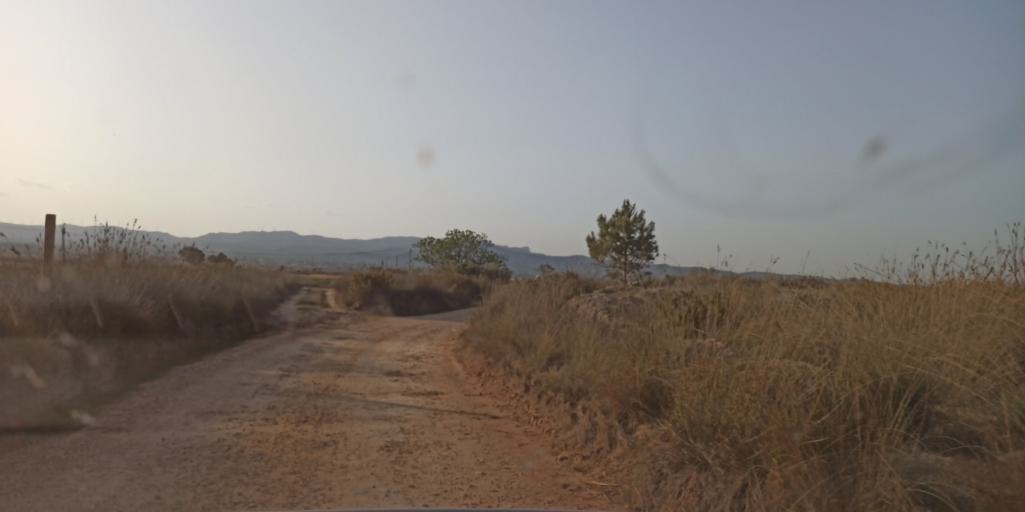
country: ES
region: Catalonia
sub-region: Provincia de Tarragona
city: L'Ampolla
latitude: 40.7817
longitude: 0.7139
